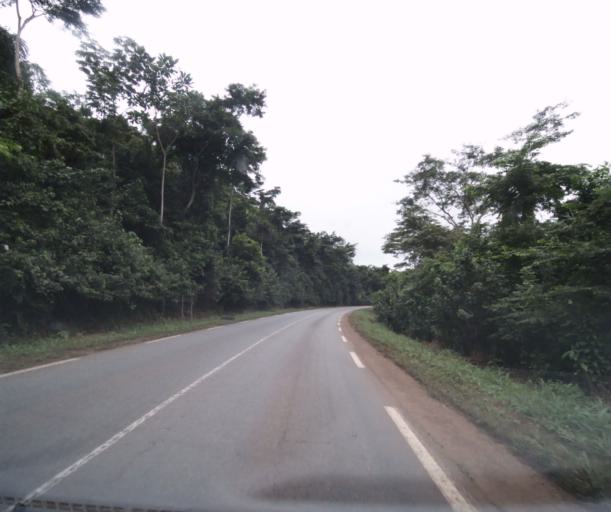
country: CM
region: Centre
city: Mbankomo
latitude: 3.7712
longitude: 11.1692
